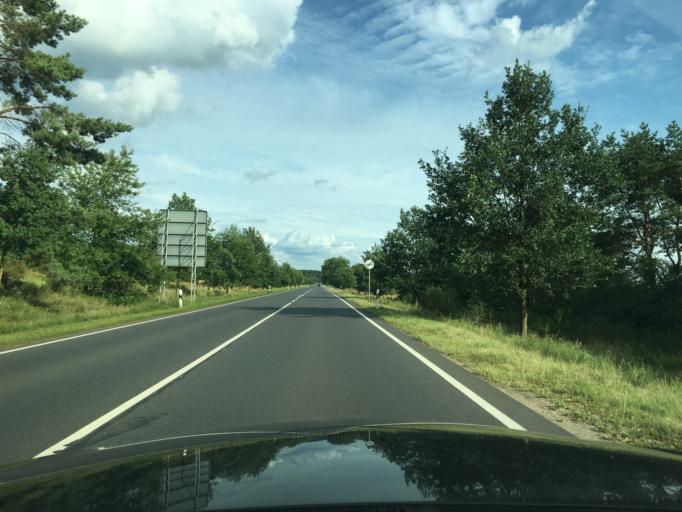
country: DE
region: Mecklenburg-Vorpommern
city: Neustrelitz
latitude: 53.3832
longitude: 13.0529
